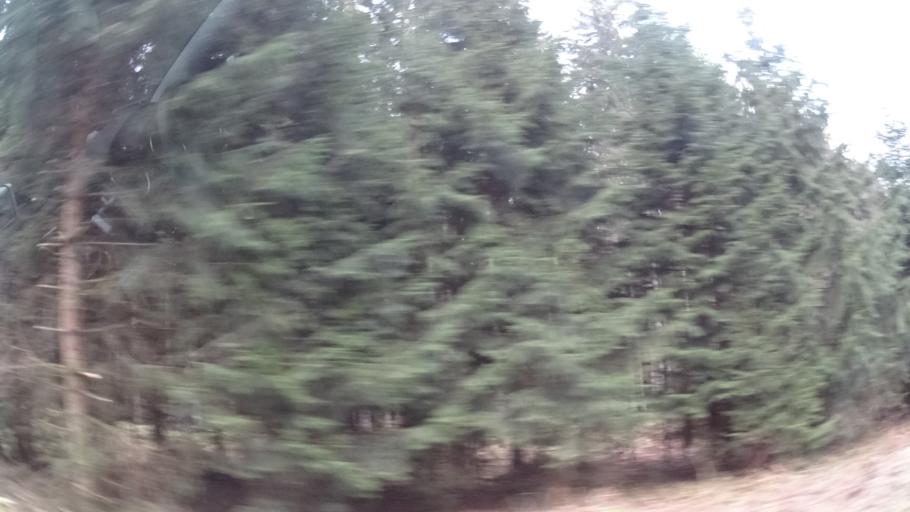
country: DE
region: Rheinland-Pfalz
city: Hattgenstein
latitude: 49.7204
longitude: 7.1549
